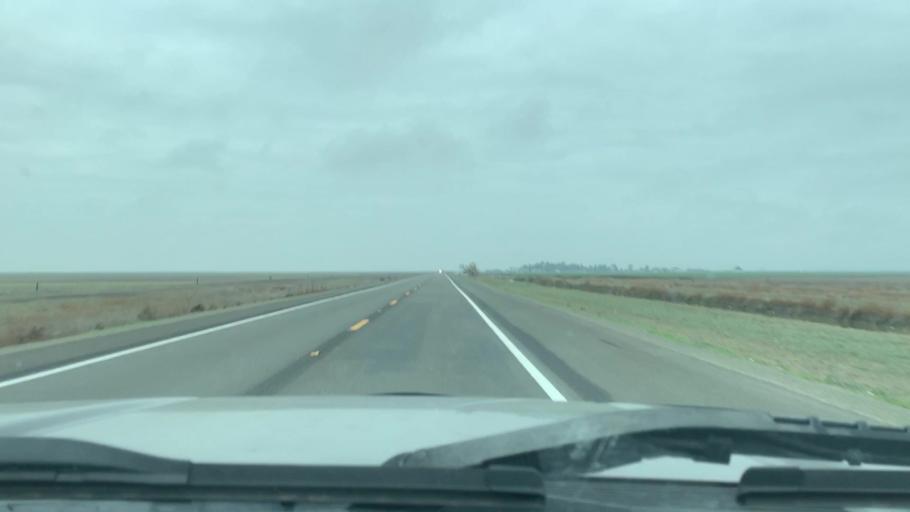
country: US
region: California
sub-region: Kings County
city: Kettleman City
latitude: 36.1061
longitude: -119.9030
